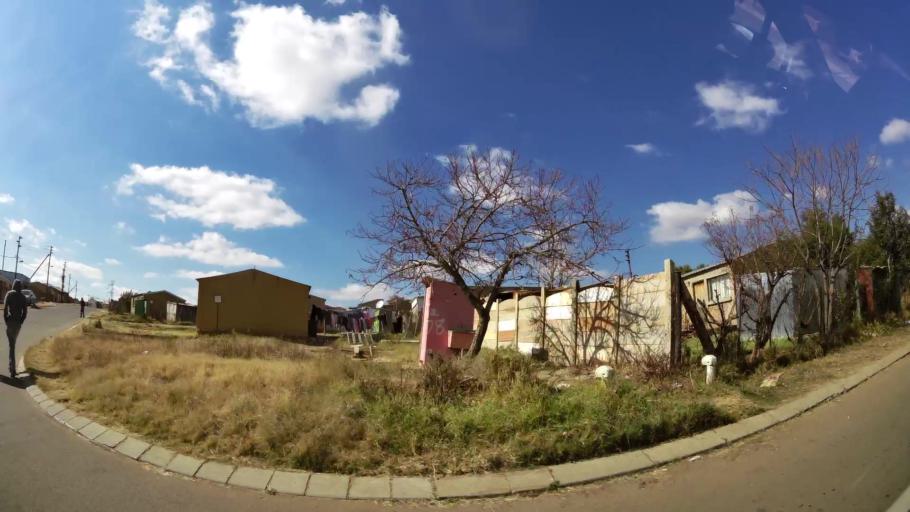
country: ZA
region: Gauteng
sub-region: West Rand District Municipality
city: Krugersdorp
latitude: -26.1414
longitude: 27.7876
